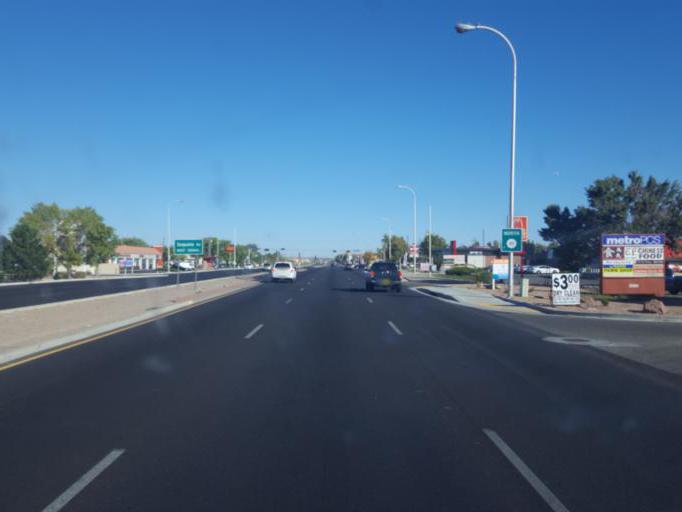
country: US
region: New Mexico
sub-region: Bernalillo County
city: Albuquerque
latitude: 35.1190
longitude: -106.7016
